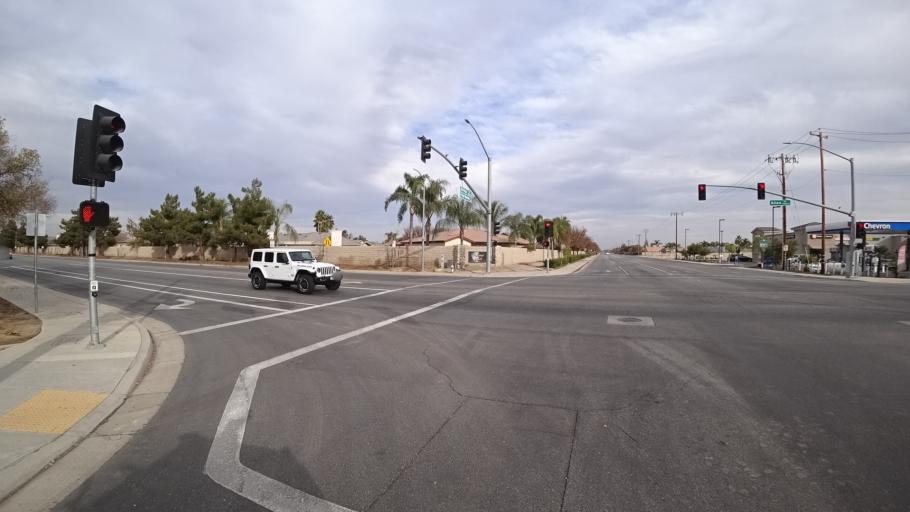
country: US
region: California
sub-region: Kern County
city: Rosedale
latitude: 35.4053
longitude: -119.1457
